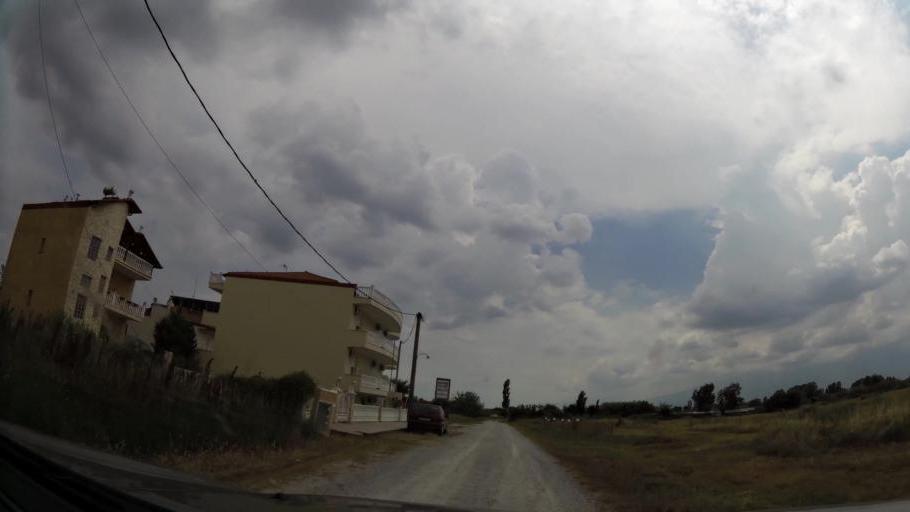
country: GR
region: Central Macedonia
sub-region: Nomos Pierias
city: Paralia
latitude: 40.2753
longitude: 22.5920
